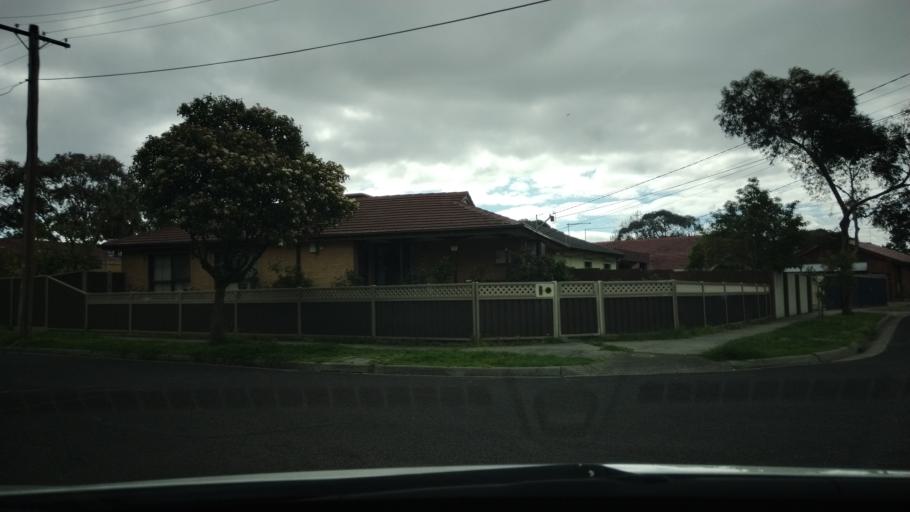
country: AU
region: Victoria
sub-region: Greater Dandenong
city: Springvale South
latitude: -37.9835
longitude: 145.1519
